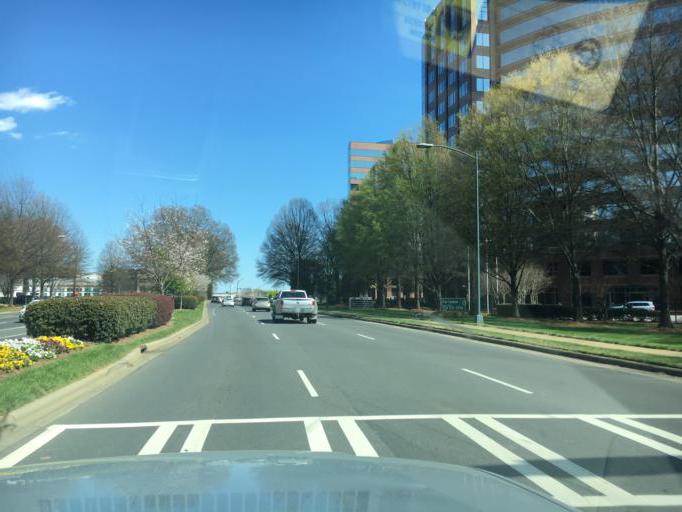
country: US
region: North Carolina
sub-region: Mecklenburg County
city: Charlotte
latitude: 35.1512
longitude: -80.8400
